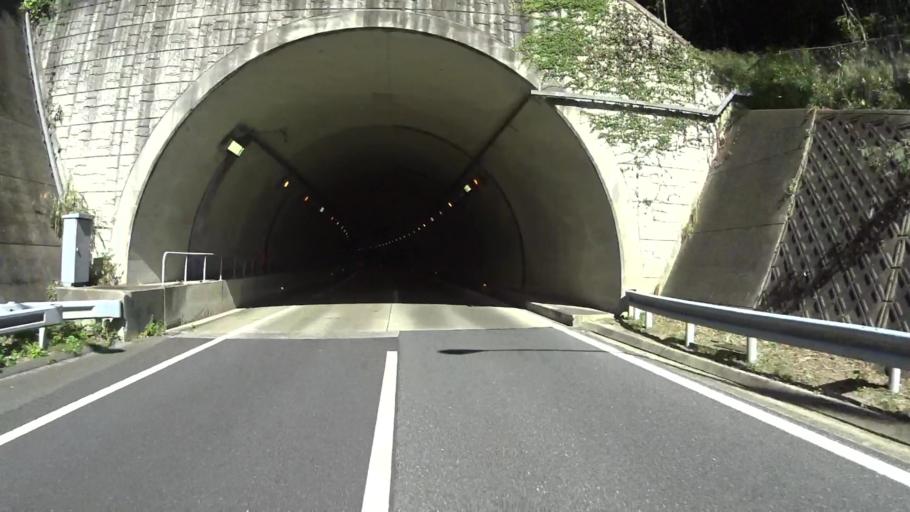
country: JP
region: Kyoto
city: Kameoka
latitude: 35.0568
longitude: 135.5341
